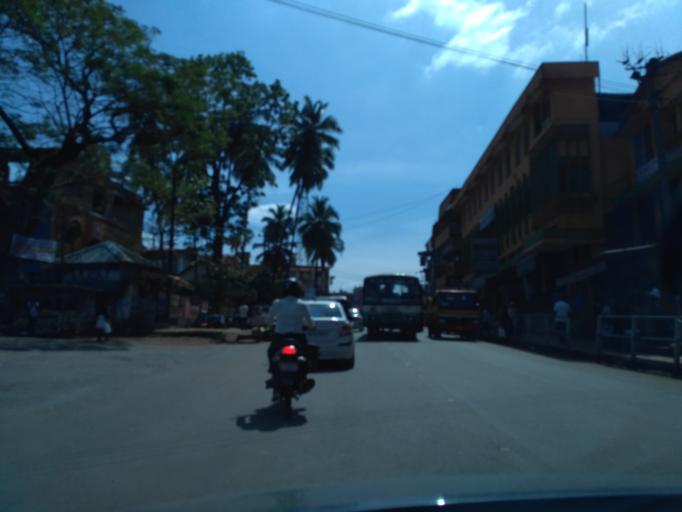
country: IN
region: Karnataka
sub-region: Dakshina Kannada
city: Sulya
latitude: 12.5570
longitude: 75.3924
